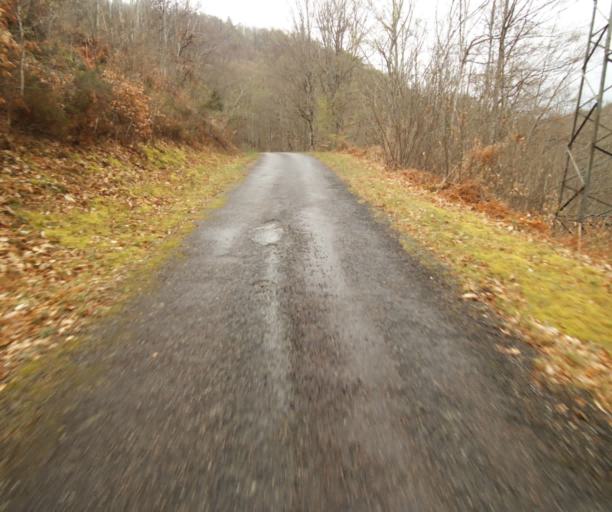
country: FR
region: Limousin
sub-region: Departement de la Correze
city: Saint-Privat
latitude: 45.2150
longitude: 2.0337
